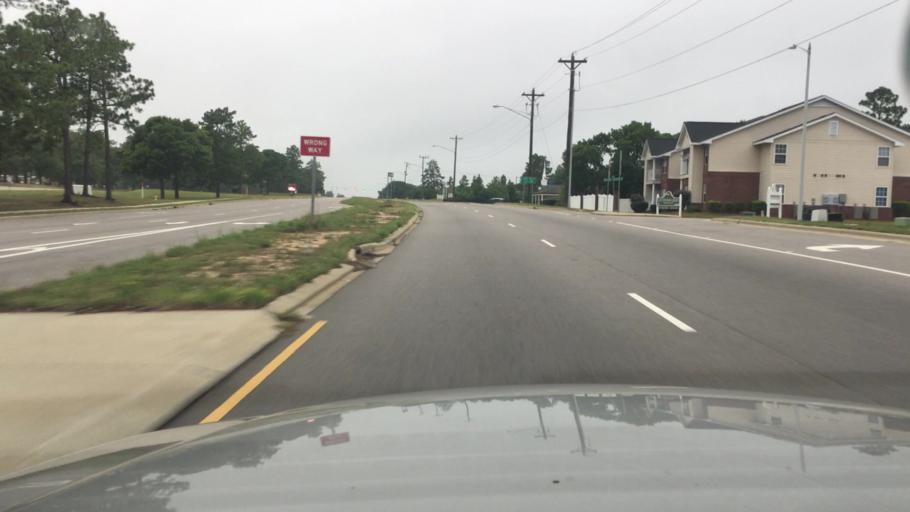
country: US
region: North Carolina
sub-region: Cumberland County
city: Hope Mills
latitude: 34.9785
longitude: -78.9243
